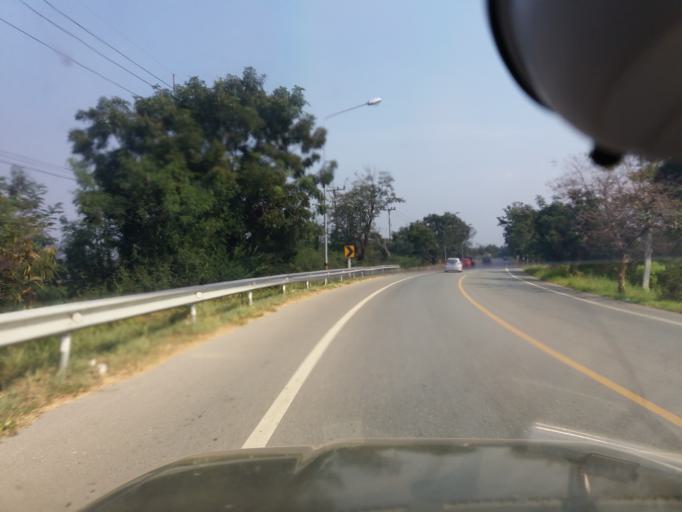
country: TH
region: Sing Buri
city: Bang Racham
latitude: 14.8831
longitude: 100.3515
